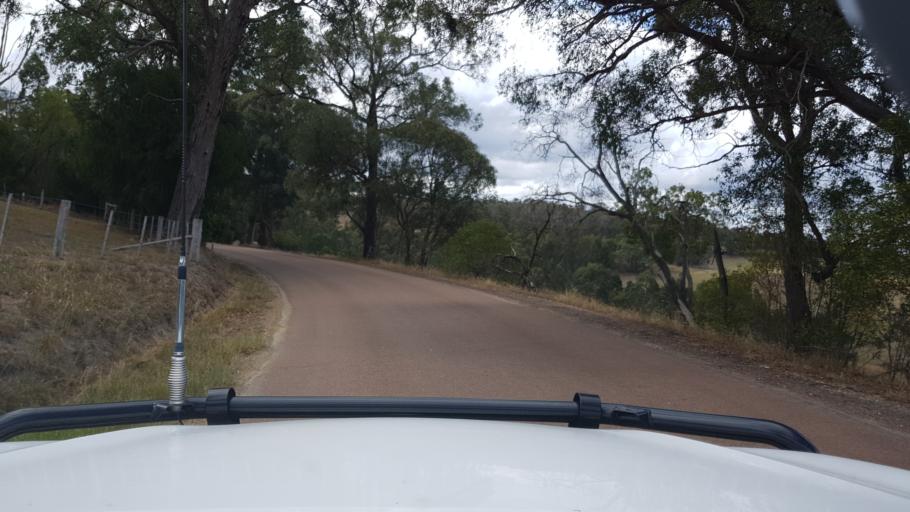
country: AU
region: Victoria
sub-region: East Gippsland
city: Bairnsdale
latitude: -37.7884
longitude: 147.5863
